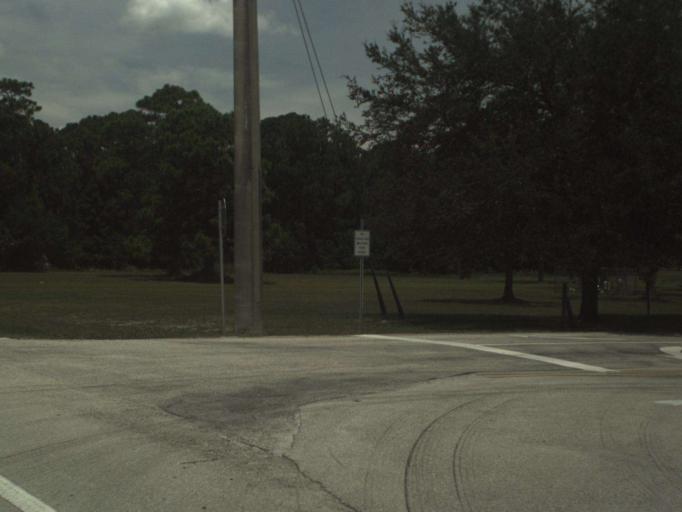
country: US
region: Florida
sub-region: Saint Lucie County
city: Lakewood Park
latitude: 27.5211
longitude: -80.4037
